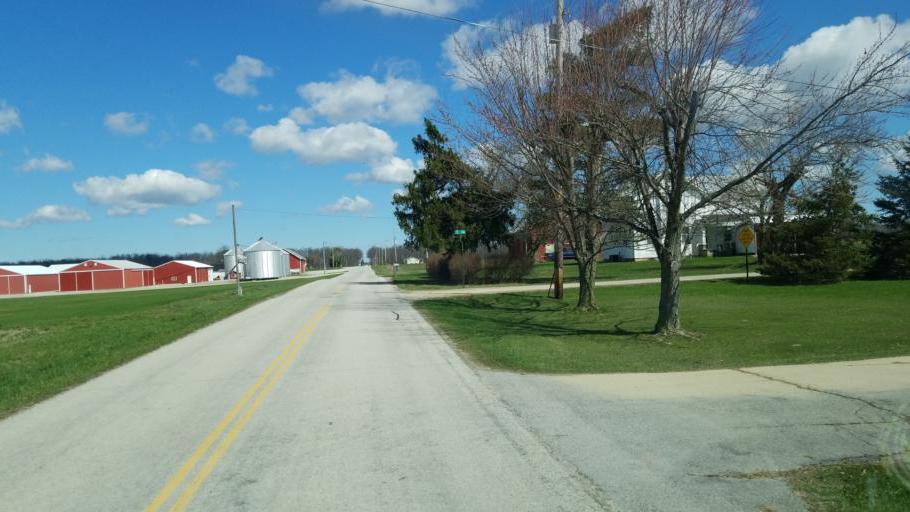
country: US
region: Ohio
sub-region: Sandusky County
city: Mount Carmel
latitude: 41.1756
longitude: -82.9382
